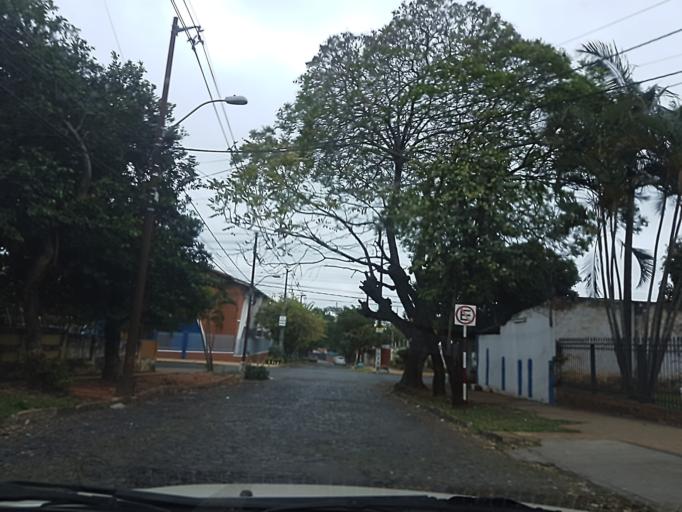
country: PY
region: Asuncion
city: Asuncion
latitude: -25.3040
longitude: -57.6050
